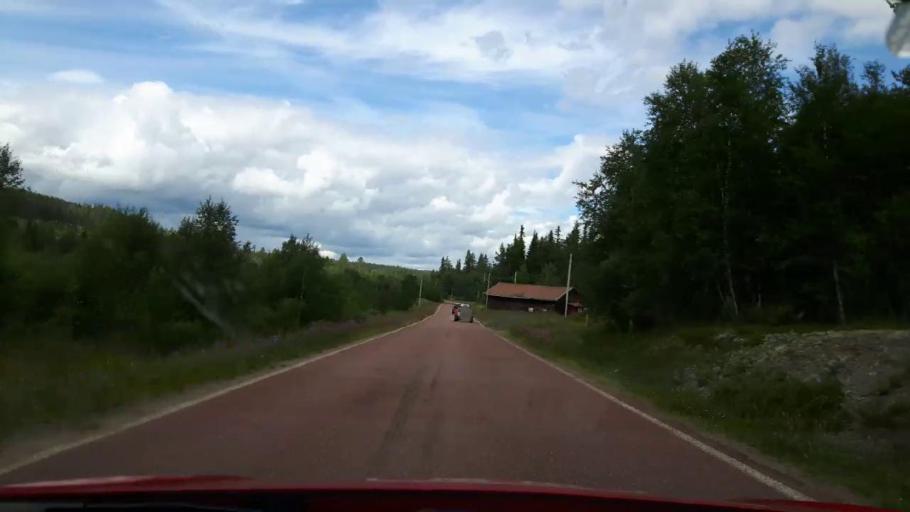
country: NO
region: Hedmark
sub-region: Trysil
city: Innbygda
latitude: 61.9965
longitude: 12.9818
